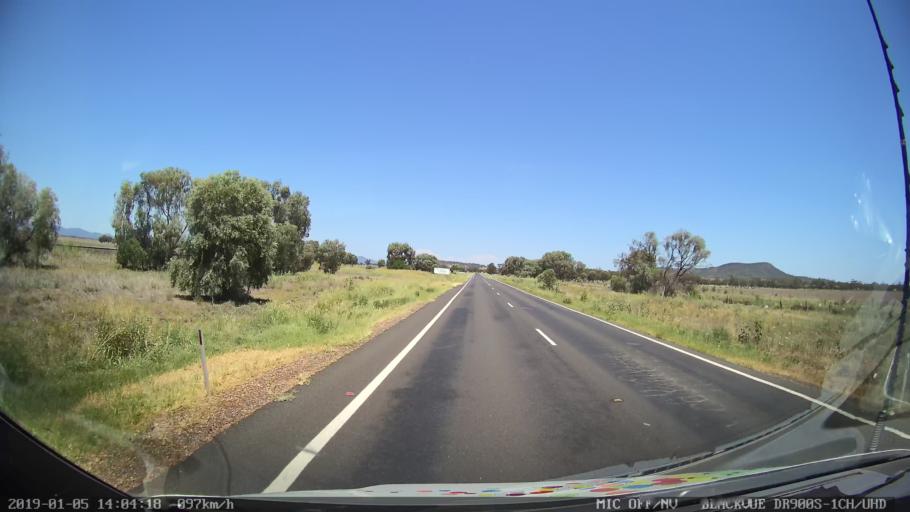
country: AU
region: New South Wales
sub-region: Gunnedah
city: Gunnedah
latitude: -31.1985
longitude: 150.3620
